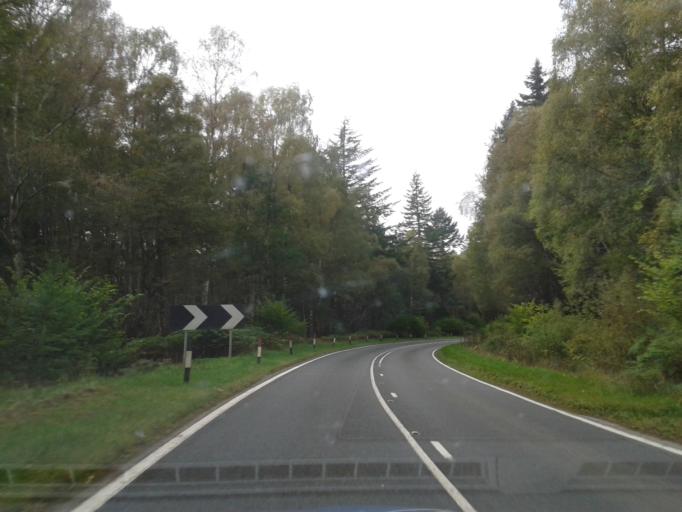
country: GB
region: Scotland
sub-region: Highland
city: Spean Bridge
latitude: 57.0657
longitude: -4.8271
